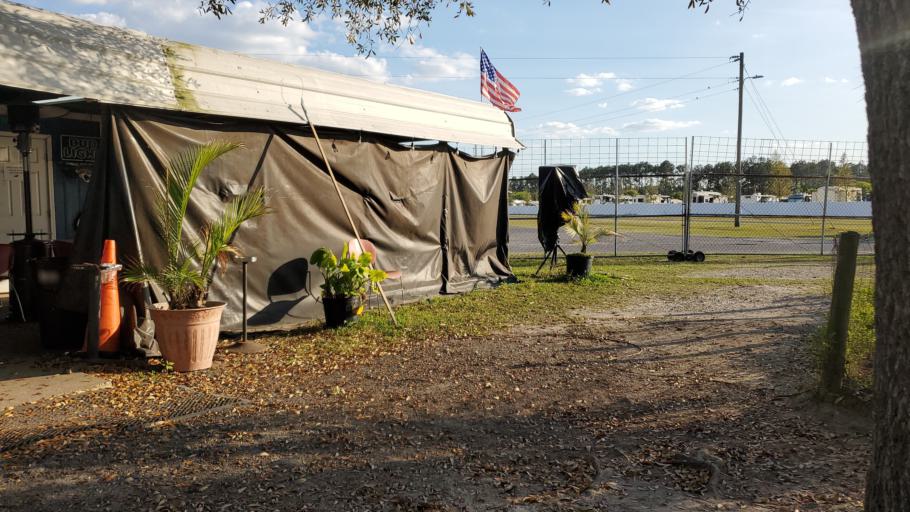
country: US
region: Florida
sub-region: Nassau County
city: Yulee
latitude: 30.5164
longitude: -81.6377
